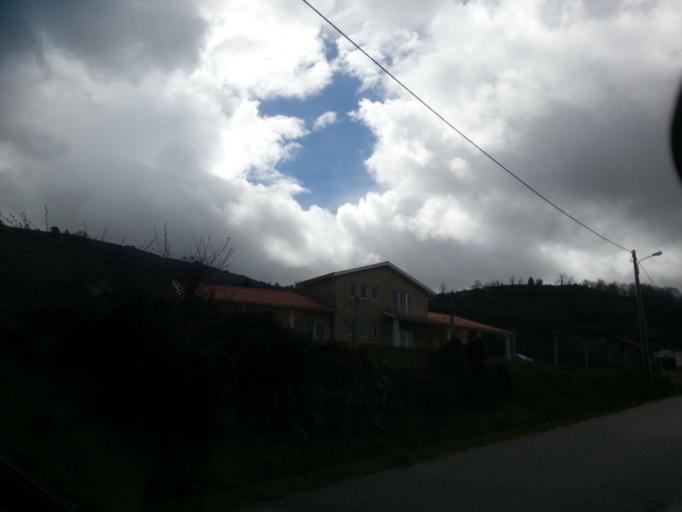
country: PT
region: Guarda
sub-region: Celorico da Beira
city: Celorico da Beira
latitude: 40.5461
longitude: -7.4562
